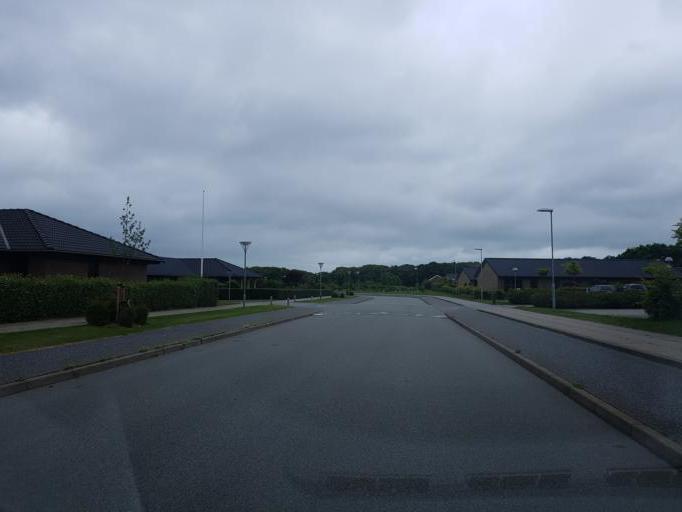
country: DK
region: South Denmark
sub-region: Varde Kommune
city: Varde
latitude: 55.6340
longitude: 8.4873
